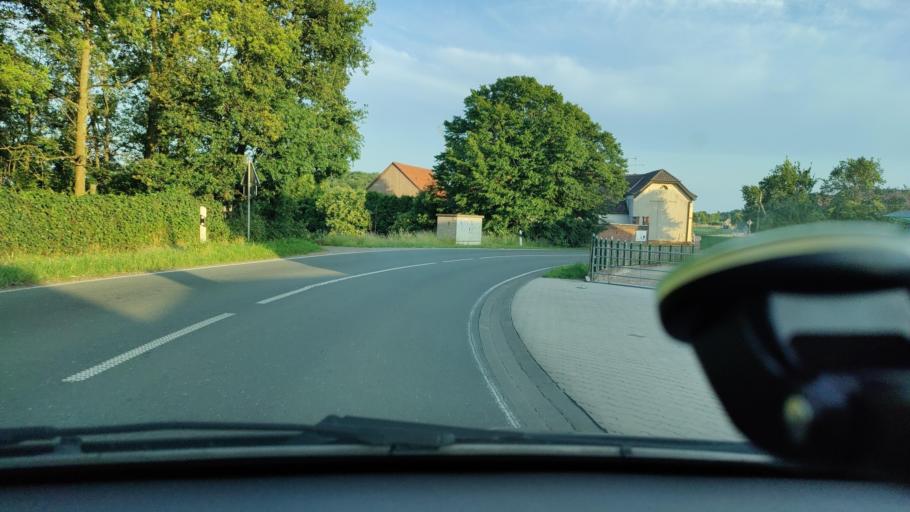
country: DE
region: North Rhine-Westphalia
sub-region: Regierungsbezirk Dusseldorf
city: Kamp-Lintfort
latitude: 51.4779
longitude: 6.5225
